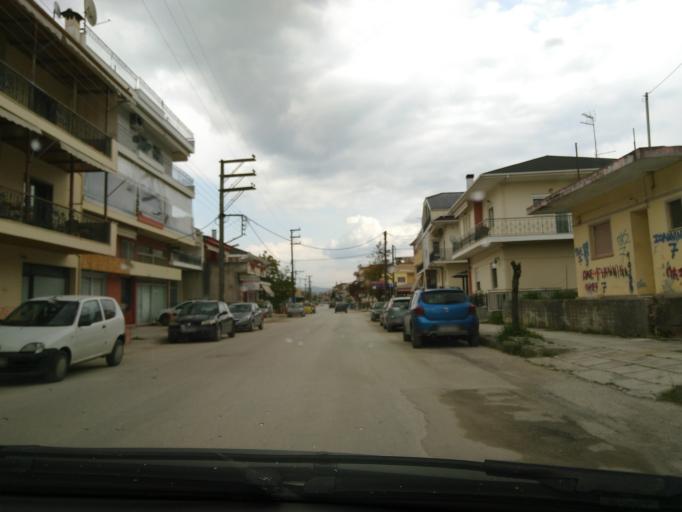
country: GR
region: Epirus
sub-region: Nomos Ioanninon
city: Anatoli
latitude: 39.6435
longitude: 20.8650
